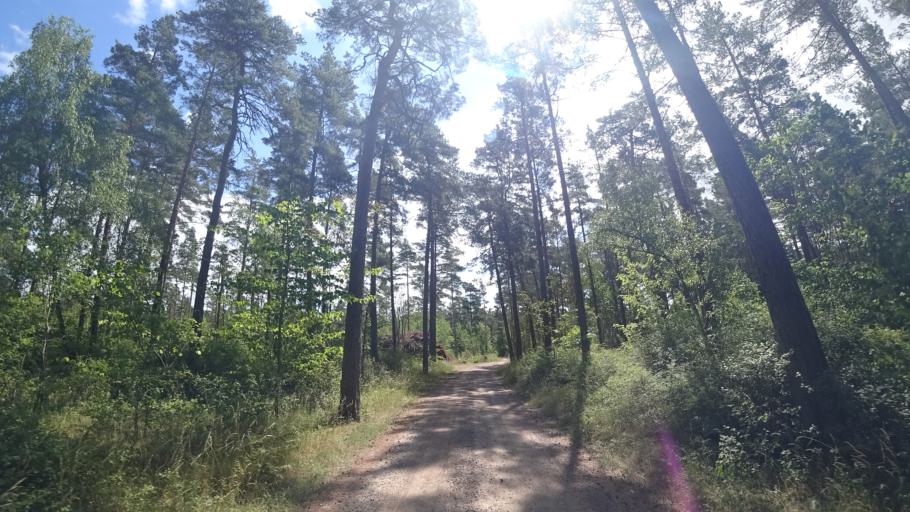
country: SE
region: Skane
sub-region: Kristianstads Kommun
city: Ahus
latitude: 55.9642
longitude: 14.2847
